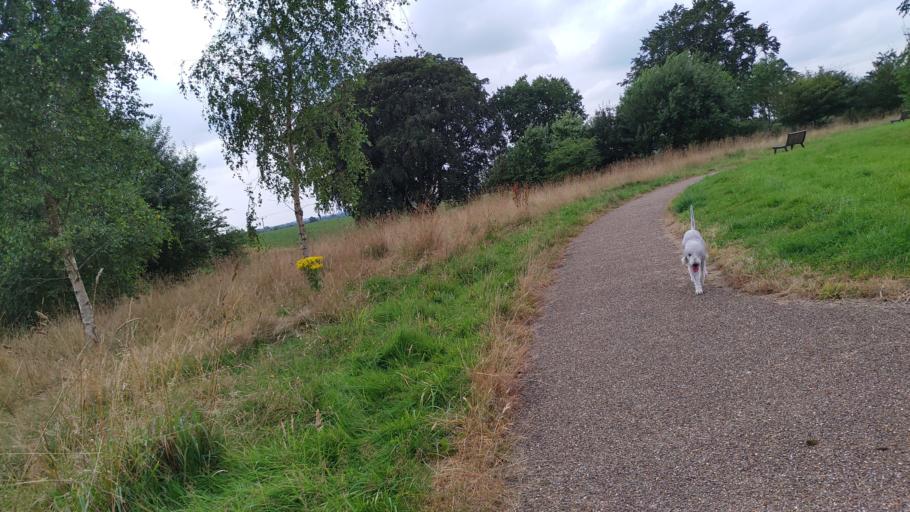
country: GB
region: England
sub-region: Lancashire
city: Coppull
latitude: 53.6289
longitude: -2.6356
